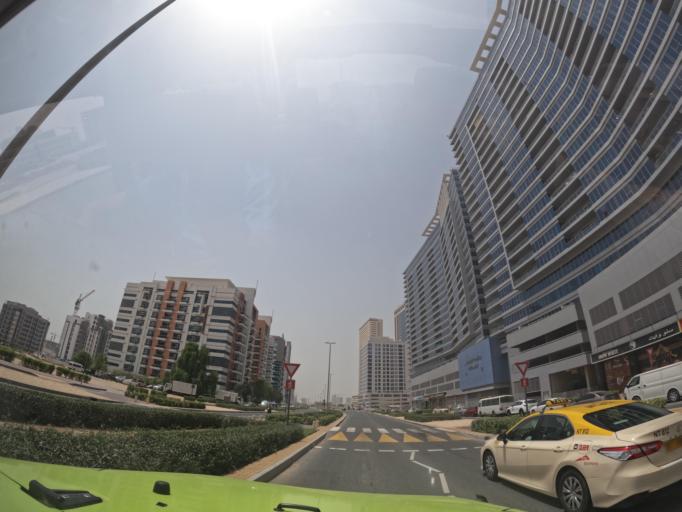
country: AE
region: Dubai
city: Dubai
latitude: 25.0906
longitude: 55.3850
